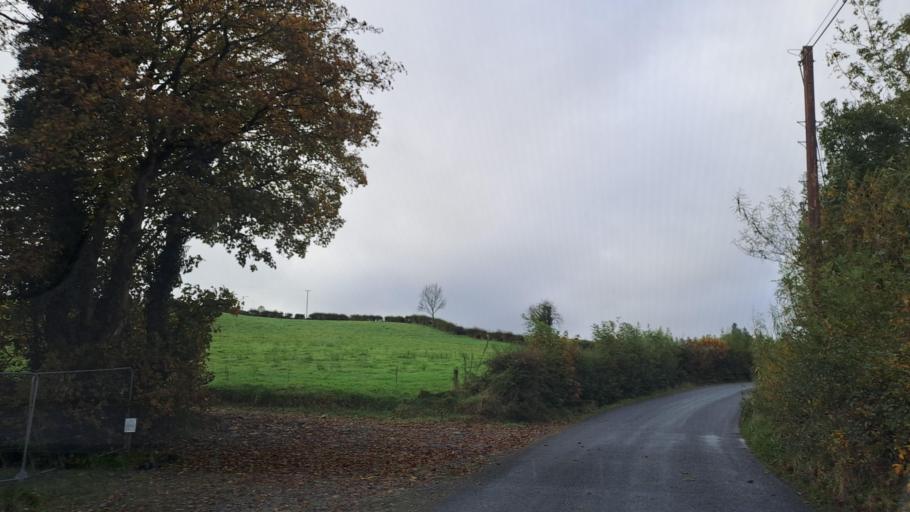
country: IE
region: Ulster
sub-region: An Cabhan
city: Bailieborough
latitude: 53.9900
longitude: -7.0090
